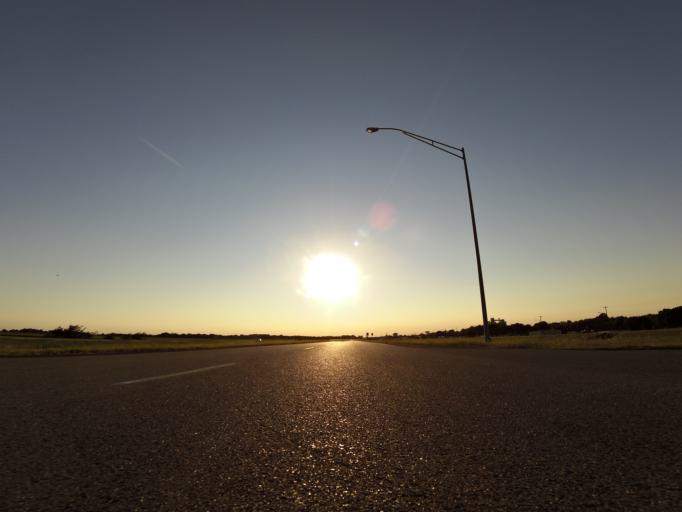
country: US
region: Kansas
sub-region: Reno County
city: Haven
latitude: 37.8951
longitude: -97.7747
